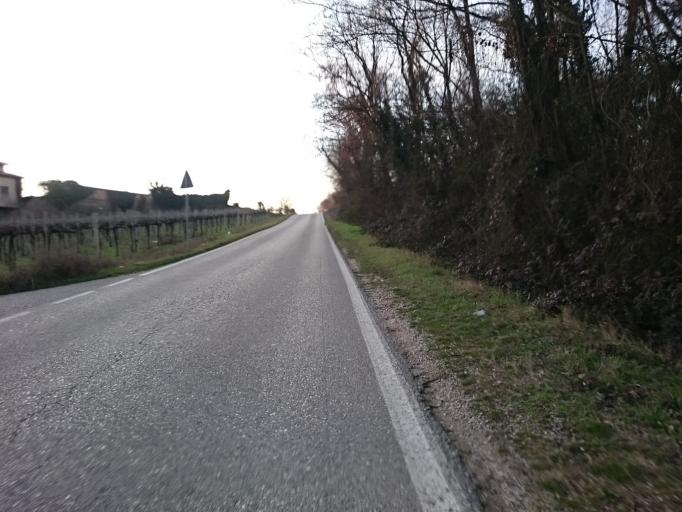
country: IT
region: Veneto
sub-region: Provincia di Verona
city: San Giorgio in Salici
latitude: 45.4280
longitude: 10.7729
